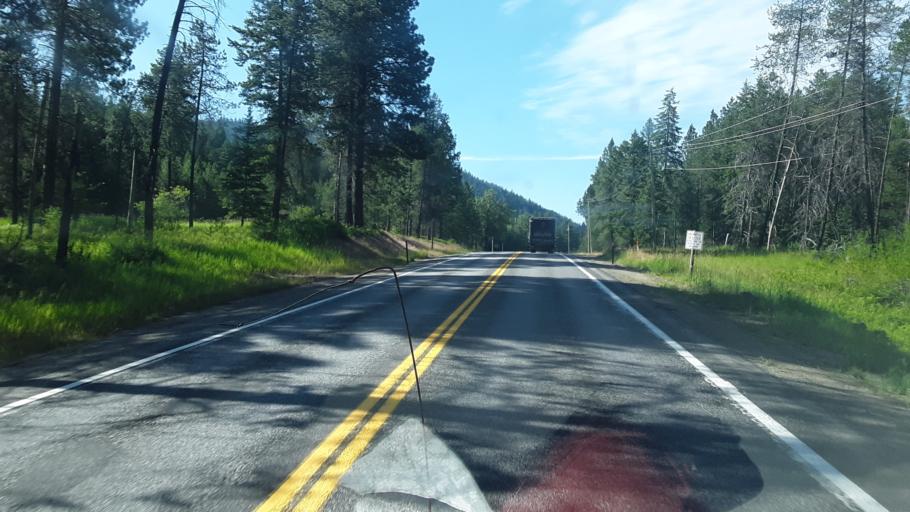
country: US
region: Idaho
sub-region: Boundary County
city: Bonners Ferry
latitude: 48.5164
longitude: -116.4437
